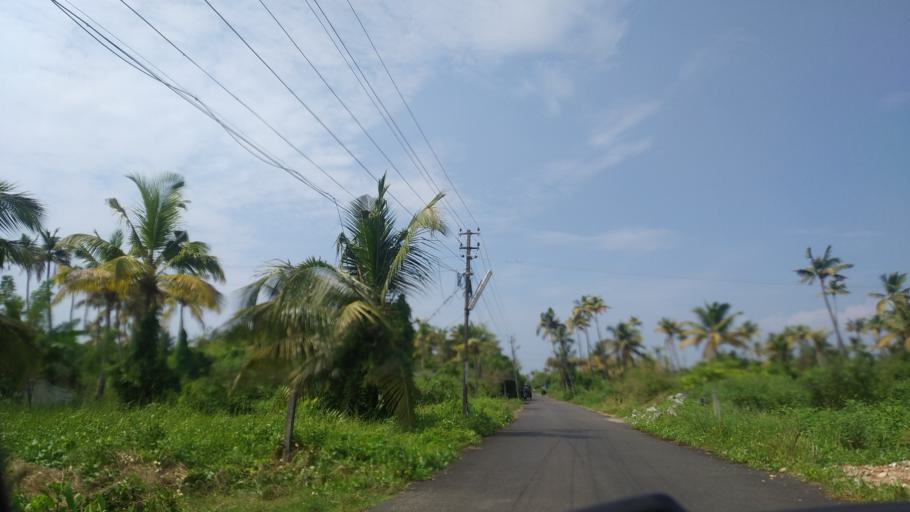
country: IN
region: Kerala
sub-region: Ernakulam
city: Elur
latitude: 10.0453
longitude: 76.2082
